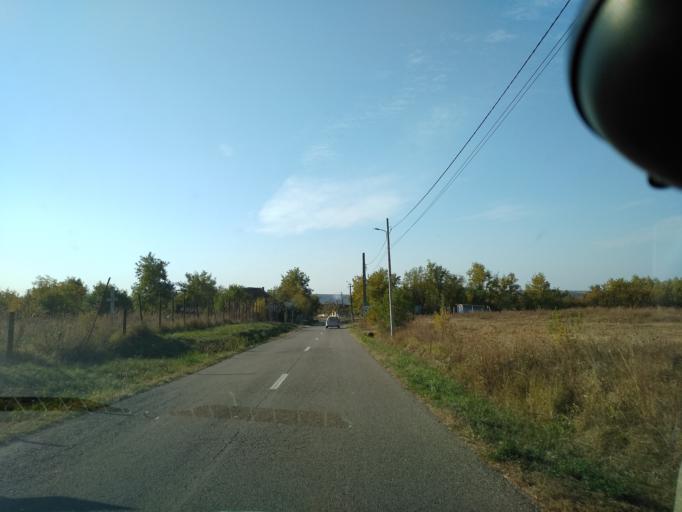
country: RO
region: Timis
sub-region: Oras Recas
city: Recas
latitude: 45.8668
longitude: 21.5153
